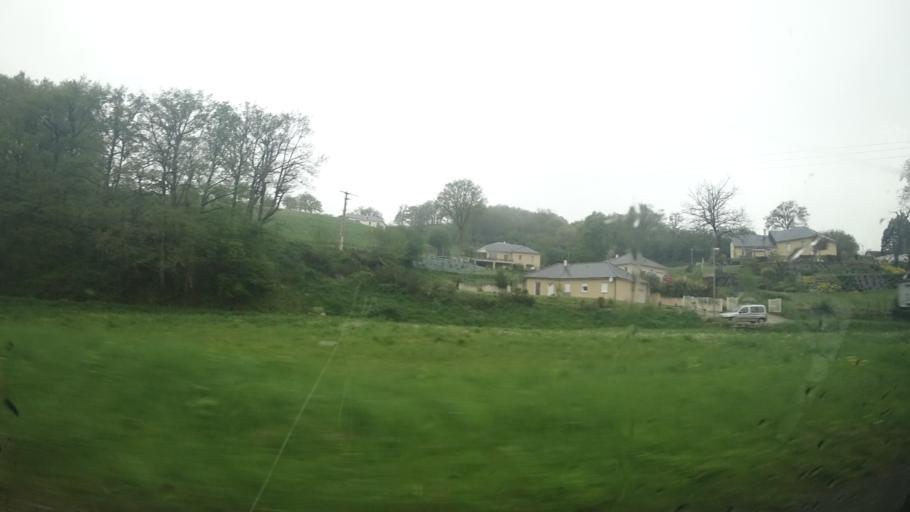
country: FR
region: Midi-Pyrenees
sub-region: Departement de l'Aveyron
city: Laissac
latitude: 44.3146
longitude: 2.8005
